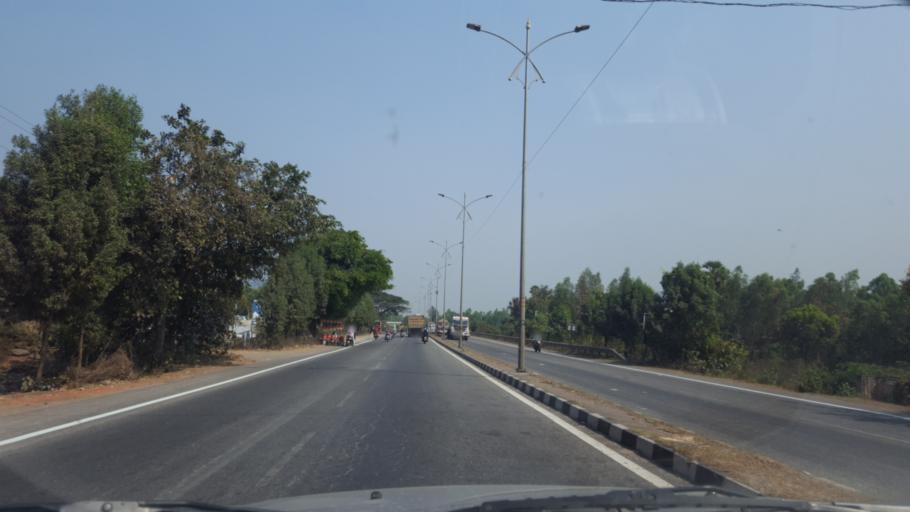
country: IN
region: Andhra Pradesh
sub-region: Vishakhapatnam
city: Anakapalle
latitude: 17.6887
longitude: 83.0672
